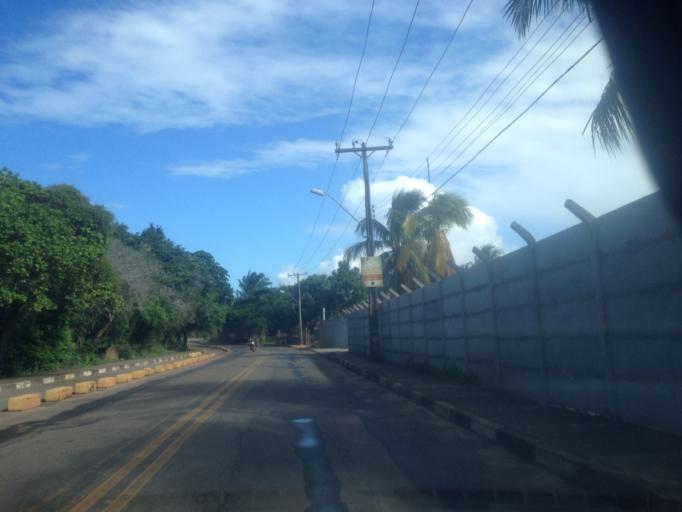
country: BR
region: Bahia
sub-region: Mata De Sao Joao
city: Mata de Sao Joao
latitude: -12.6013
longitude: -38.0405
